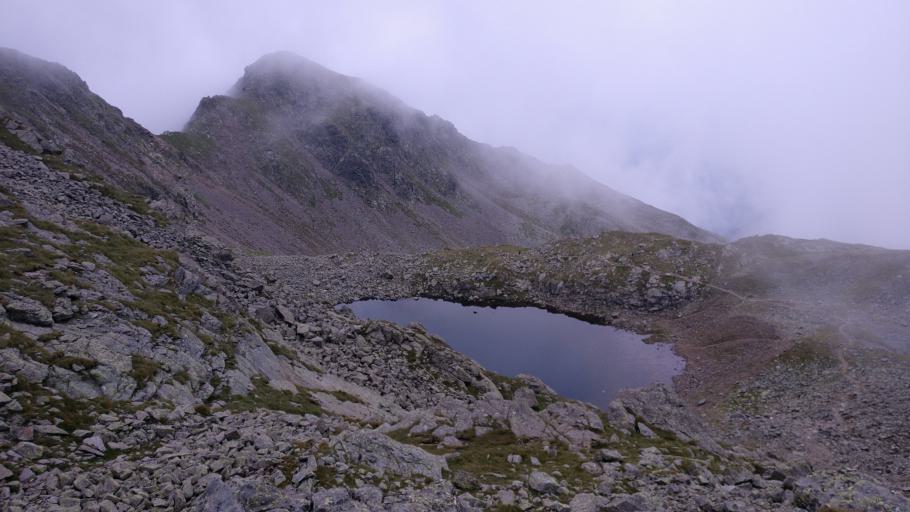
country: IT
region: Trentino-Alto Adige
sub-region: Bolzano
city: Villandro - Villanders
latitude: 46.7078
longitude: 11.4940
